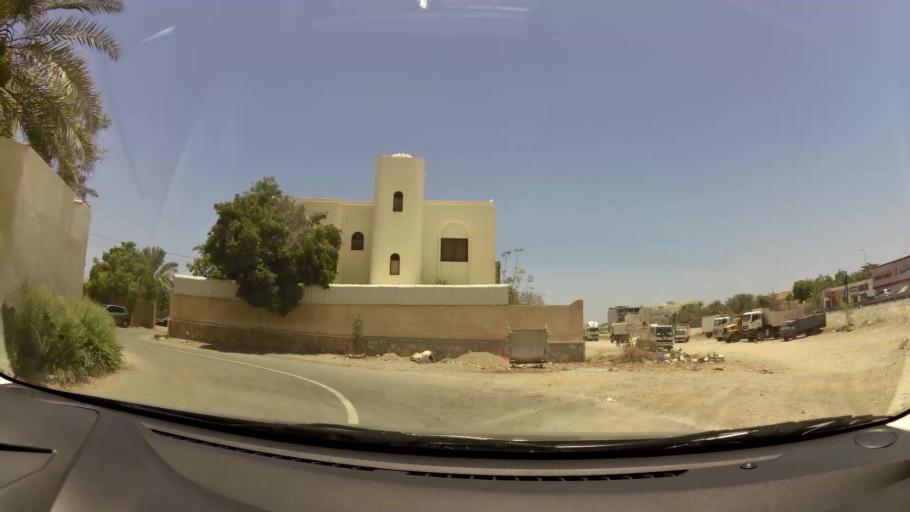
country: OM
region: Muhafazat Masqat
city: As Sib al Jadidah
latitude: 23.6362
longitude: 58.2316
